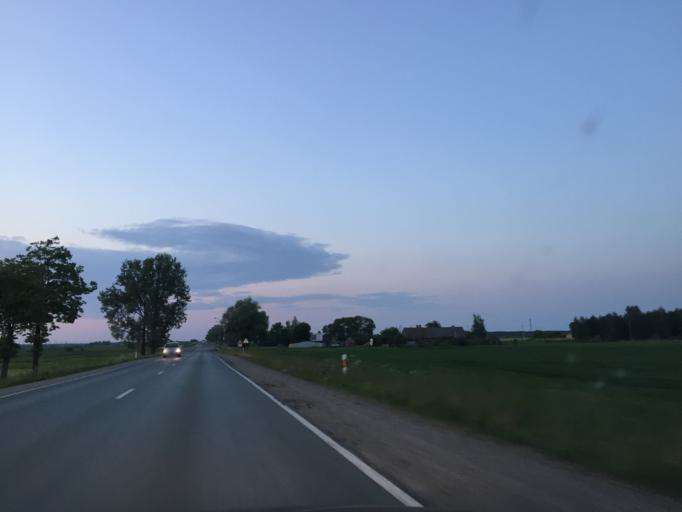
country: LT
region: Siauliu apskritis
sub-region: Siauliai
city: Siauliai
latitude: 56.0728
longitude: 23.4529
